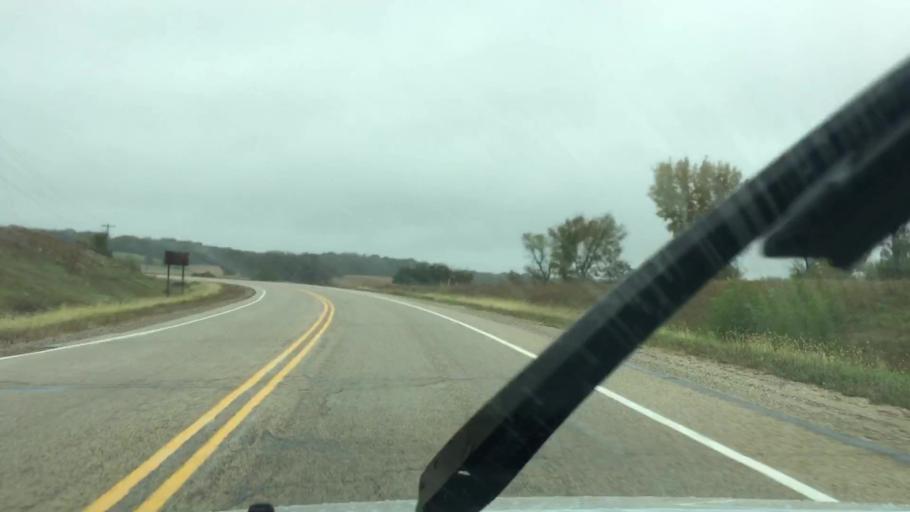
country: US
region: Wisconsin
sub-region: Jefferson County
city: Palmyra
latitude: 42.8850
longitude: -88.5616
